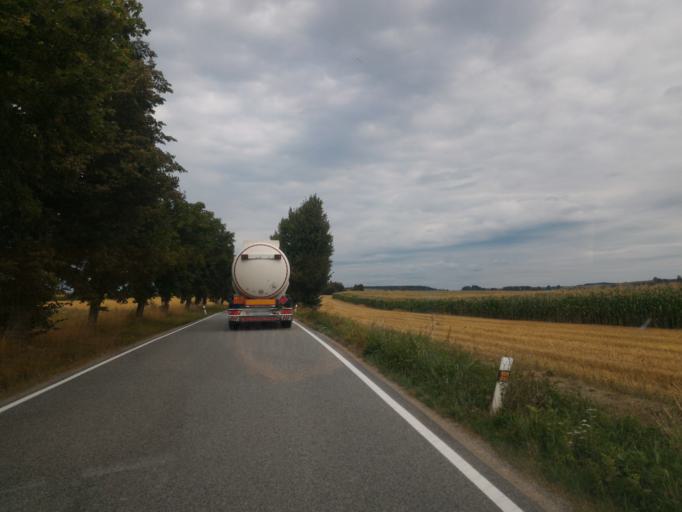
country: CZ
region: Vysocina
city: Zeletava
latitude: 49.1685
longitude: 15.5868
